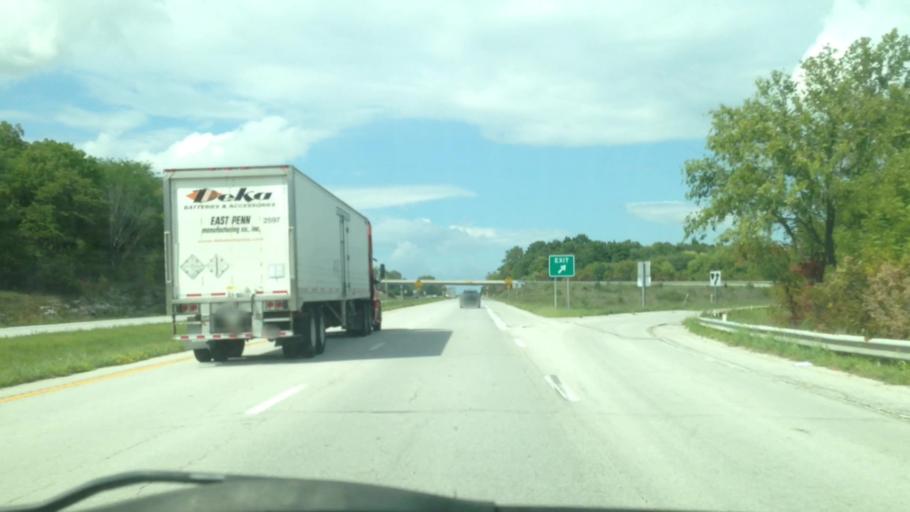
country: US
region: Missouri
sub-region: Marion County
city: Palmyra
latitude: 39.7649
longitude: -91.5191
